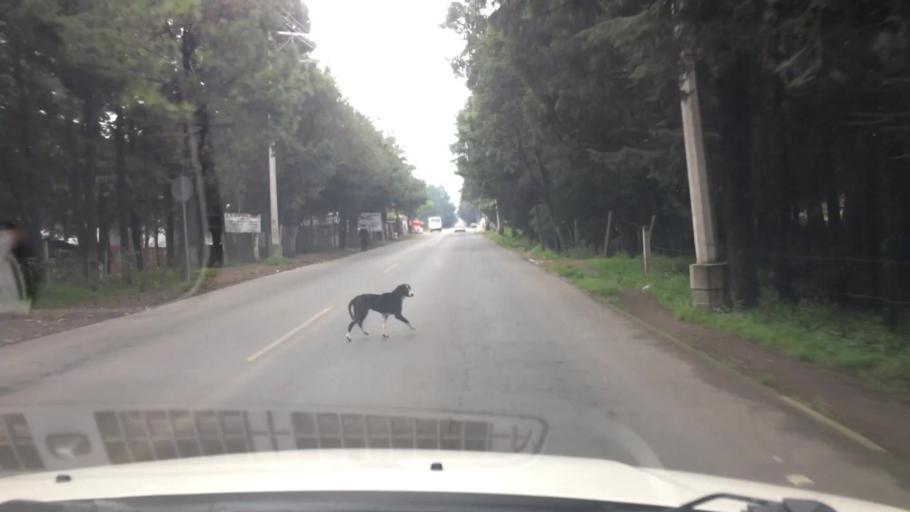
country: MX
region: Mexico City
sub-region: Tlalpan
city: Lomas de Tepemecatl
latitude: 19.2394
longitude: -99.2368
